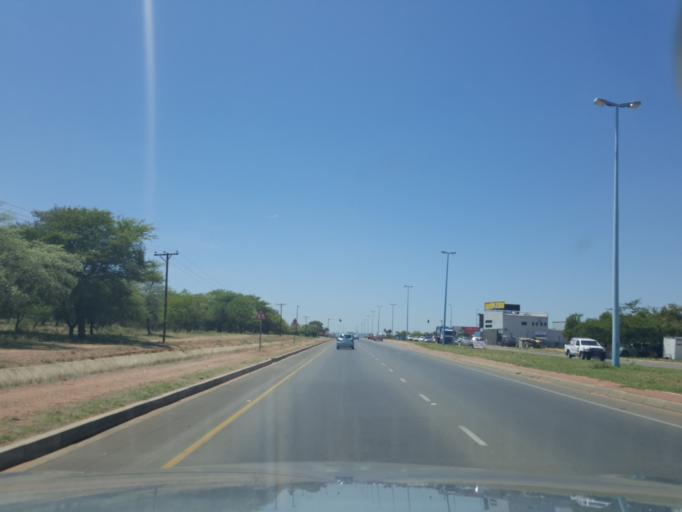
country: BW
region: Kweneng
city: Mogoditshane
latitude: -24.6052
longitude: 25.8568
